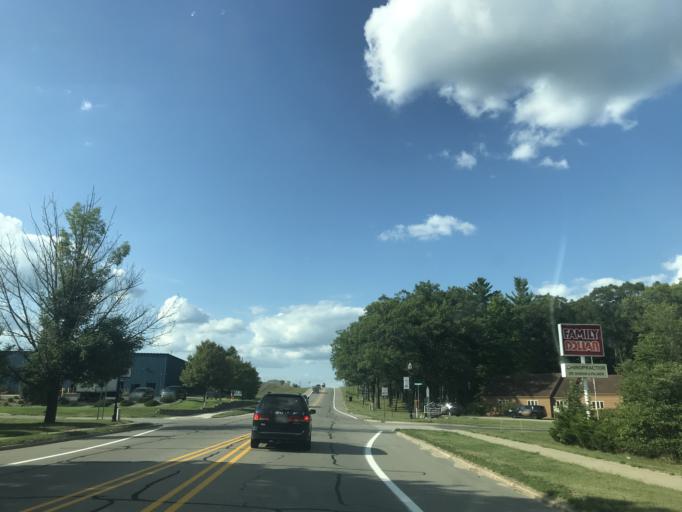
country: US
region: Michigan
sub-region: Newaygo County
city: White Cloud
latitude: 43.5533
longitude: -85.7716
